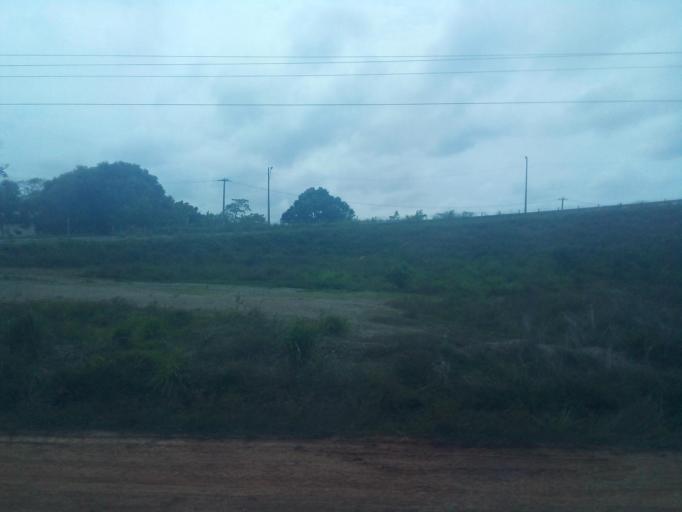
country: BR
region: Maranhao
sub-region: Anajatuba
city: Anajatuba
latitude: -3.3501
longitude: -44.5042
